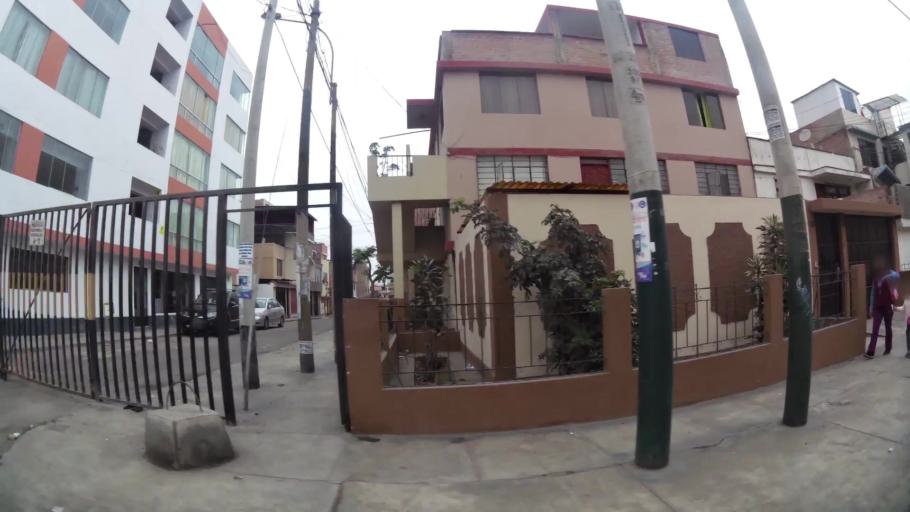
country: PE
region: Lima
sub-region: Lima
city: Surco
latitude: -12.1693
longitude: -76.9740
